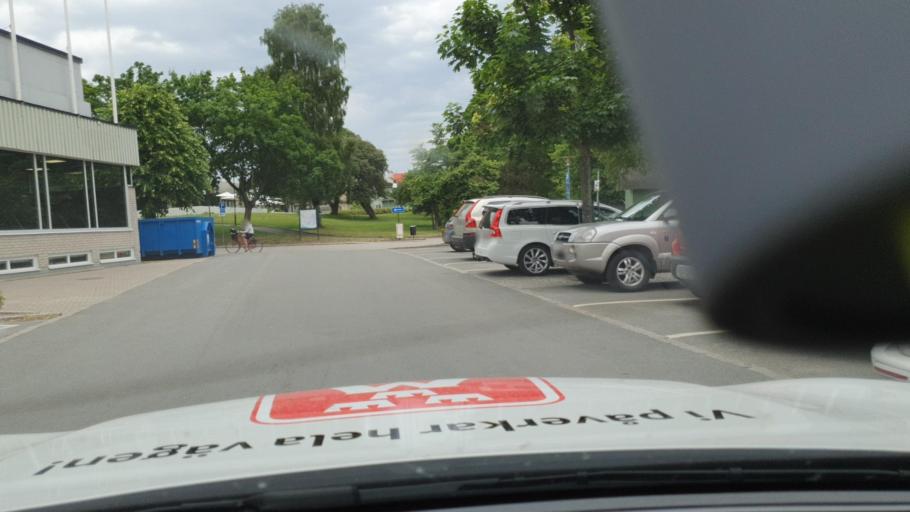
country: SE
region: Vaestra Goetaland
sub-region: Hjo Kommun
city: Hjo
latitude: 58.3029
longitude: 14.2921
